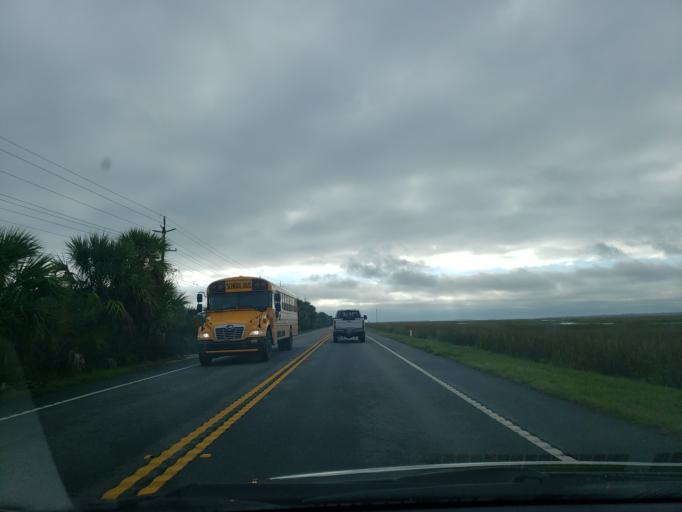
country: US
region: Georgia
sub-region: Chatham County
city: Wilmington Island
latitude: 32.0282
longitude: -80.9263
